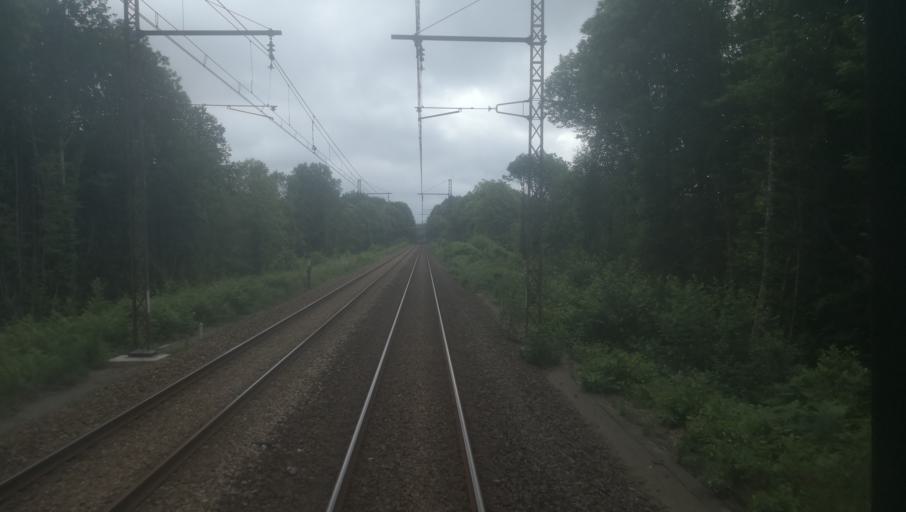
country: FR
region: Limousin
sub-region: Departement de la Haute-Vienne
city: Ambazac
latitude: 45.9622
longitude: 1.4384
